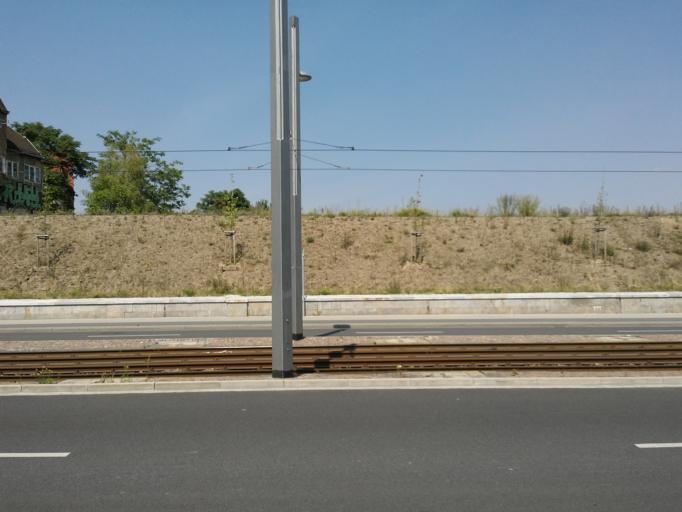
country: DE
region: Saxony
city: Leipzig
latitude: 51.3522
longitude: 12.3847
